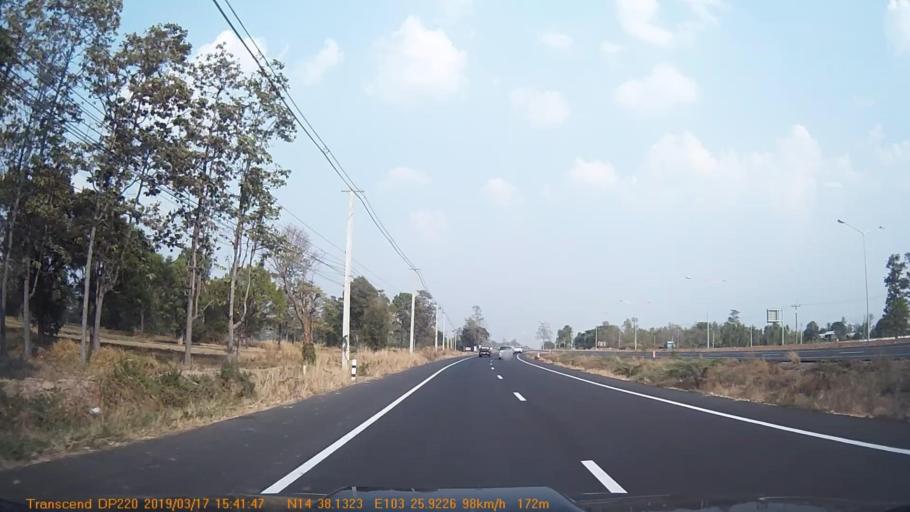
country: TH
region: Surin
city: Prasat
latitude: 14.6354
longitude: 103.4323
